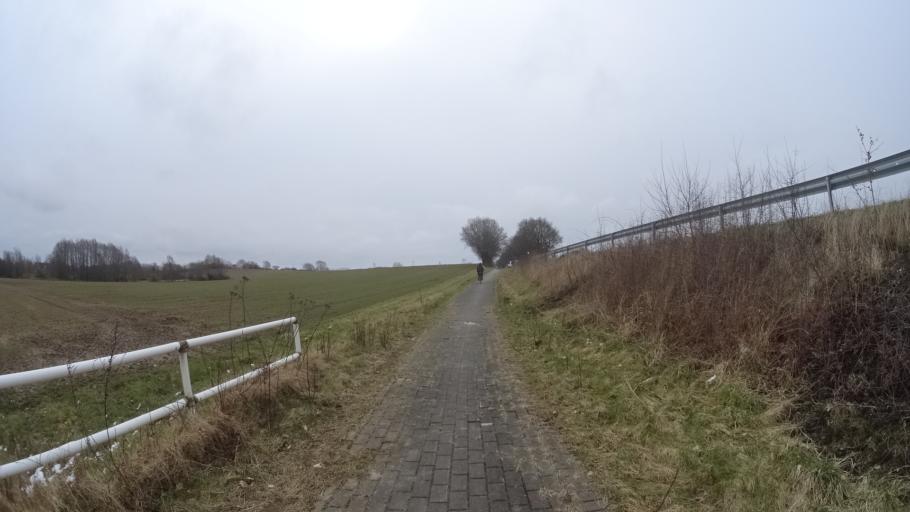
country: DE
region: Schleswig-Holstein
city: Trondel
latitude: 54.3558
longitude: 10.5416
